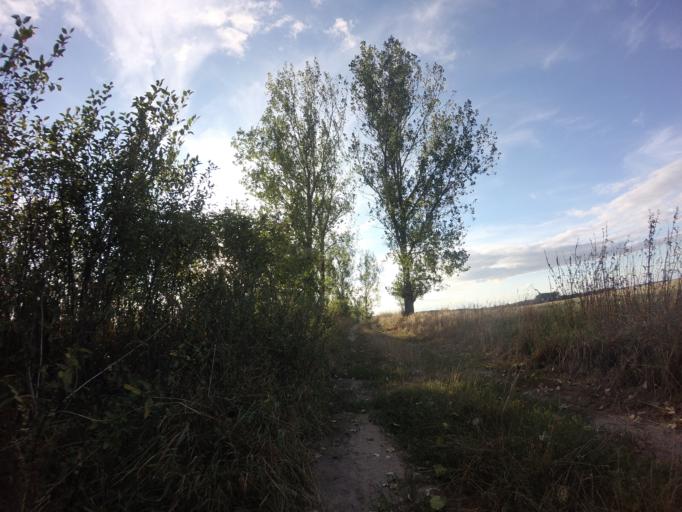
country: PL
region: West Pomeranian Voivodeship
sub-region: Powiat choszczenski
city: Choszczno
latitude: 53.1153
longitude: 15.4301
